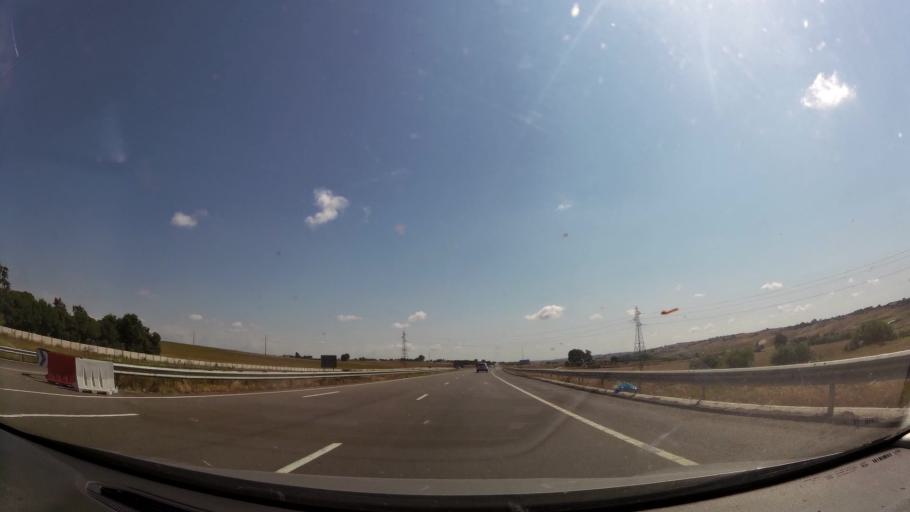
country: MA
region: Rabat-Sale-Zemmour-Zaer
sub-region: Rabat
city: Rabat
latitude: 33.9603
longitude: -6.7454
